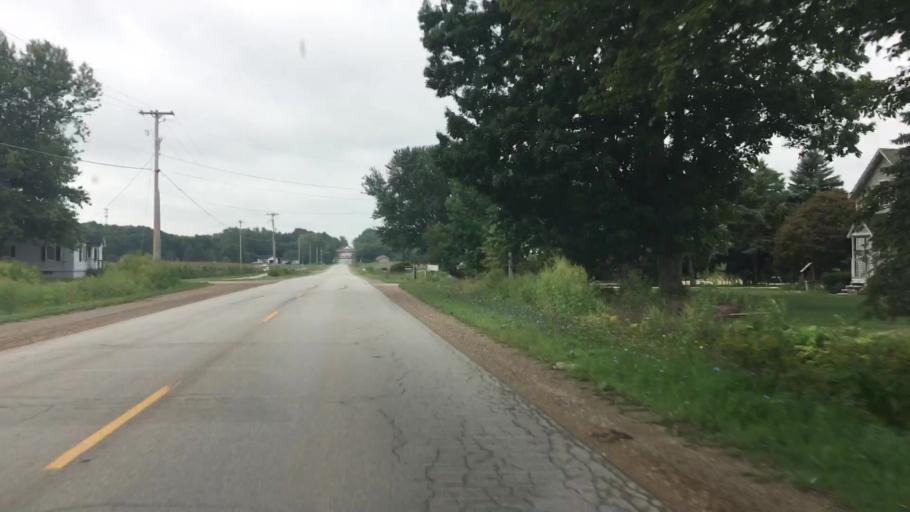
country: US
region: Michigan
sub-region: Ottawa County
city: Hudsonville
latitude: 42.8652
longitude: -85.8365
